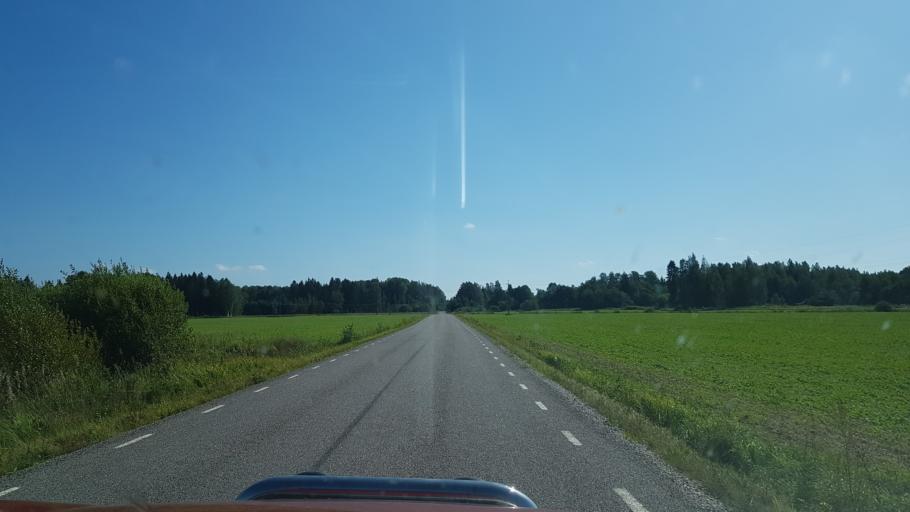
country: EE
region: Polvamaa
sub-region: Polva linn
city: Polva
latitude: 58.2158
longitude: 27.2173
